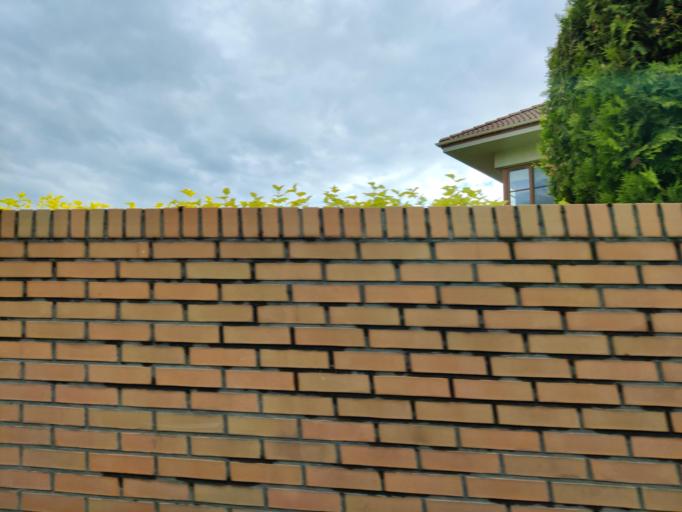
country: PL
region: Masovian Voivodeship
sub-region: Powiat piaseczynski
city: Konstancin-Jeziorna
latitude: 52.1122
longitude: 21.1229
